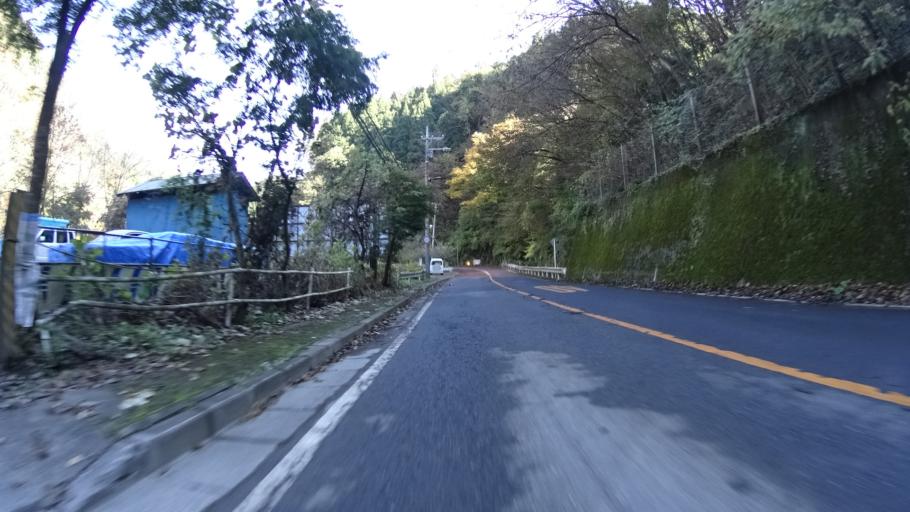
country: JP
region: Yamanashi
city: Uenohara
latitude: 35.7192
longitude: 139.0668
